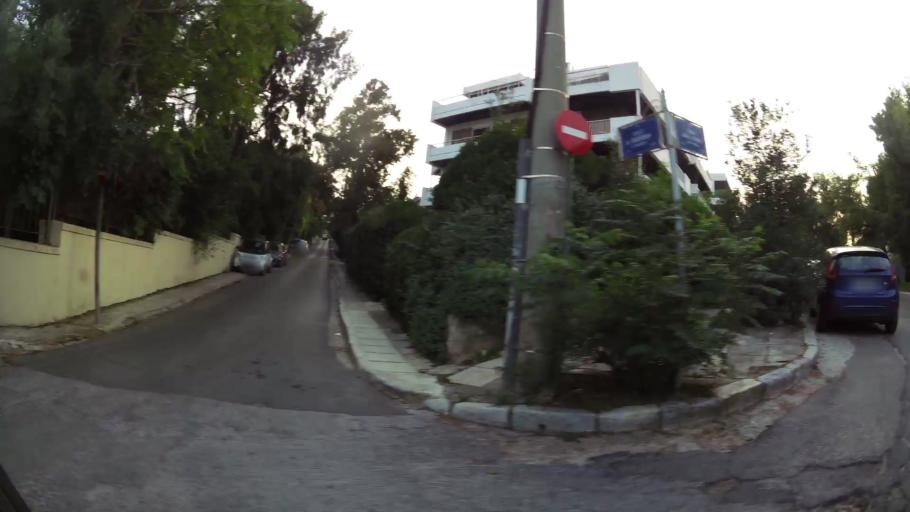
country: GR
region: Attica
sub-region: Nomarchia Athinas
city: Psychiko
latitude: 38.0193
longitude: 23.7771
